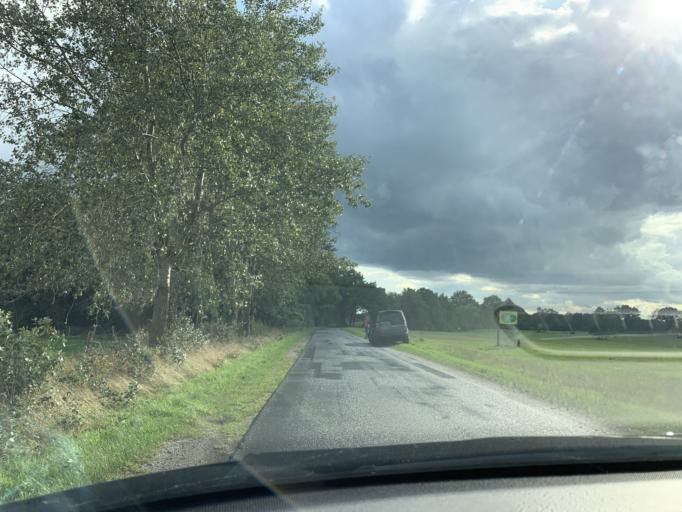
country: DE
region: Lower Saxony
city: Westerstede
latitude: 53.3105
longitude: 7.9754
